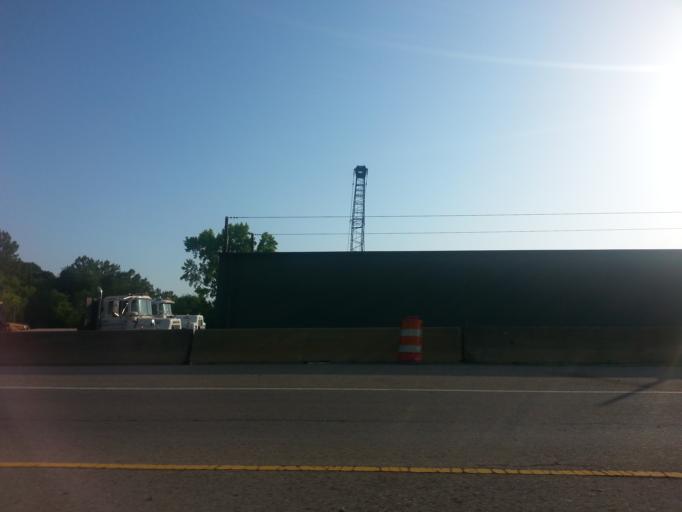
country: US
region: Tennessee
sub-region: Loudon County
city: Lenoir City
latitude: 35.7785
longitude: -84.2417
